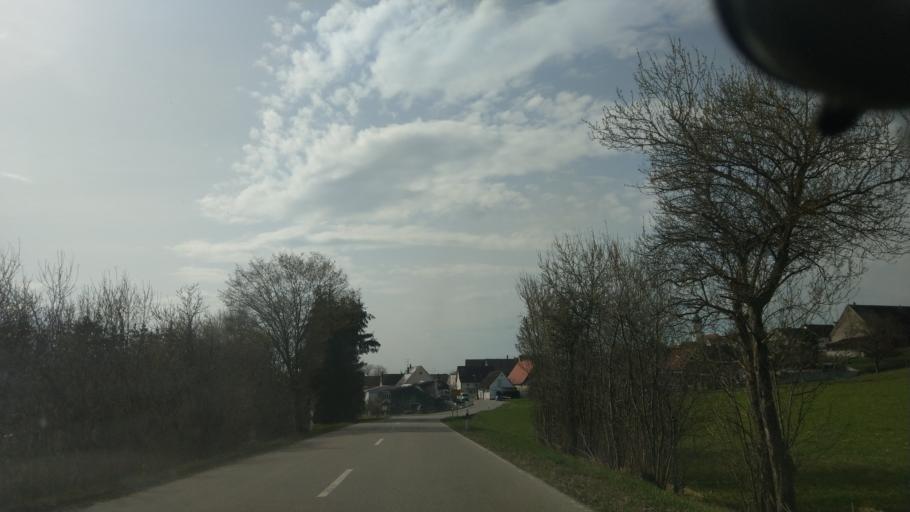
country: DE
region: Baden-Wuerttemberg
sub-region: Tuebingen Region
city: Ollingen
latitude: 48.5271
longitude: 10.1518
